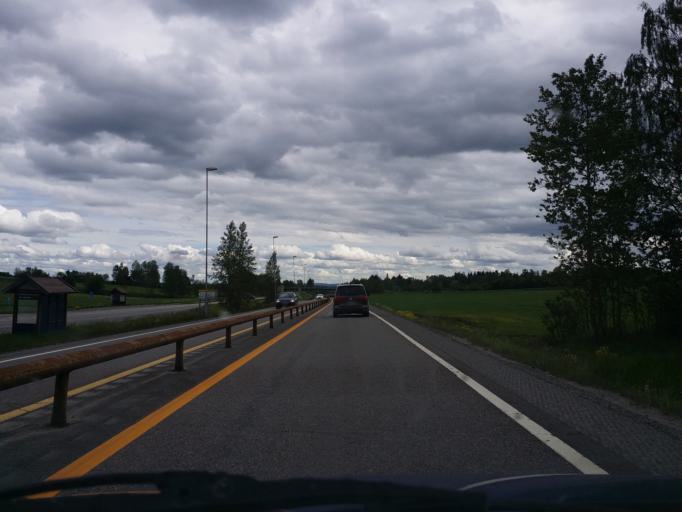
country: NO
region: Hedmark
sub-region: Hamar
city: Hamar
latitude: 60.8509
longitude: 11.0138
